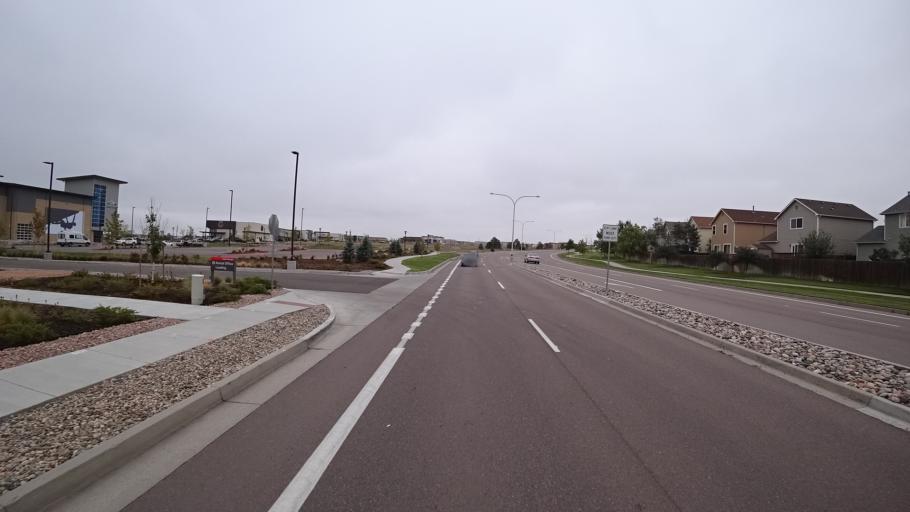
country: US
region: Colorado
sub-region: El Paso County
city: Cimarron Hills
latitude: 38.9217
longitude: -104.7172
